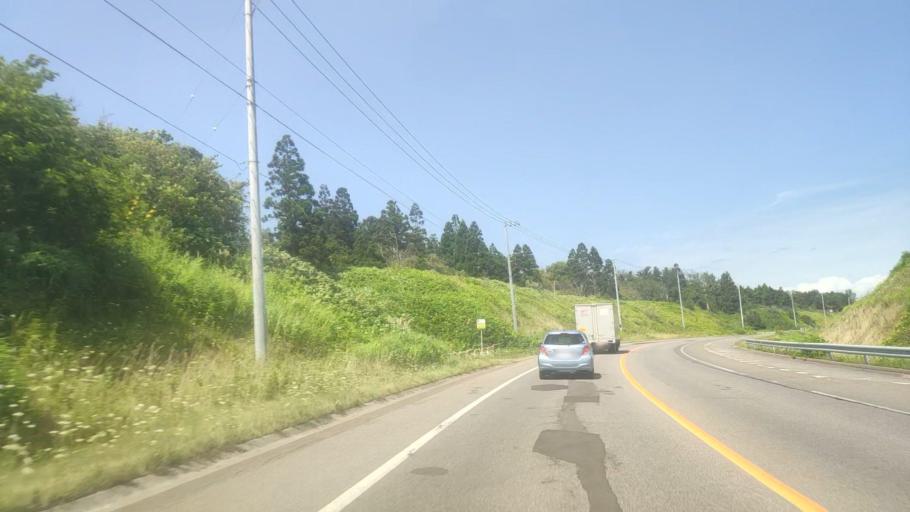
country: JP
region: Hokkaido
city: Nanae
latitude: 42.2010
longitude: 140.4086
